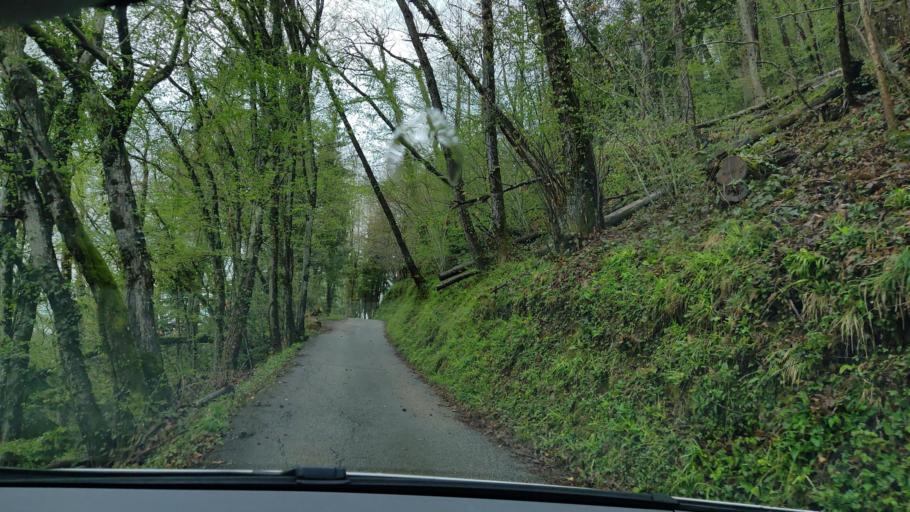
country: FR
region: Rhone-Alpes
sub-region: Departement de la Savoie
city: Vimines
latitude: 45.5547
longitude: 5.8118
